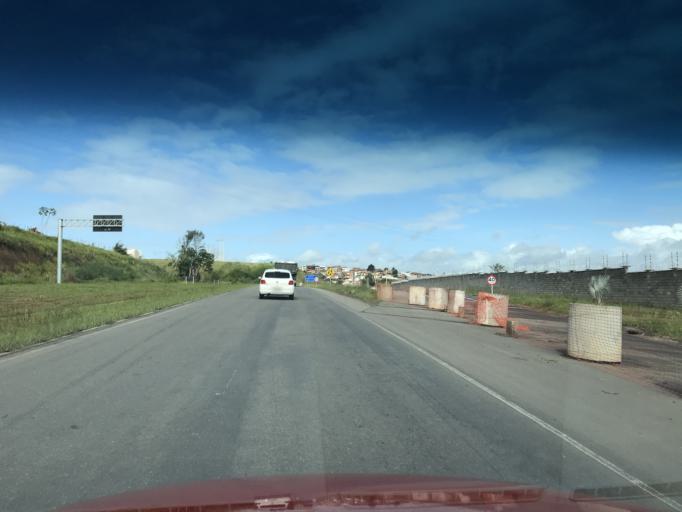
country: BR
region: Bahia
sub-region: Santo Antonio De Jesus
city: Santo Antonio de Jesus
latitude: -12.9520
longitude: -39.2550
